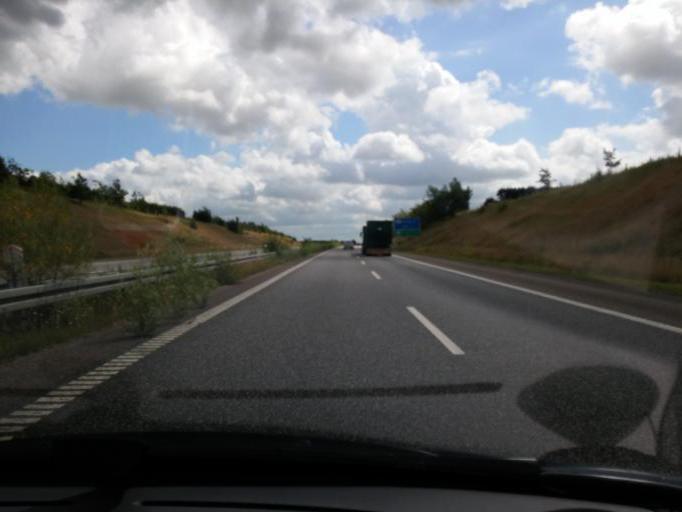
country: DK
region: South Denmark
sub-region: Faaborg-Midtfyn Kommune
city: Arslev
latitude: 55.2748
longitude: 10.4609
